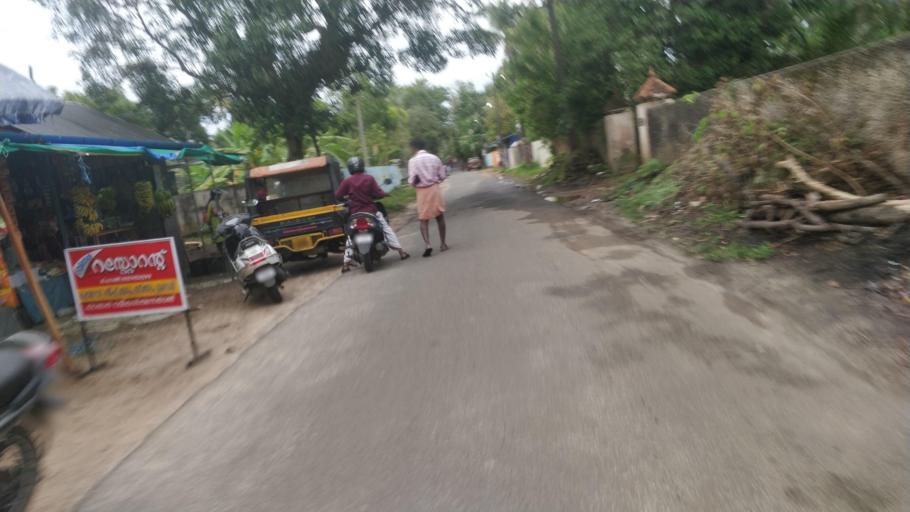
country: IN
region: Kerala
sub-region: Alappuzha
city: Shertallai
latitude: 9.6970
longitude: 76.3473
